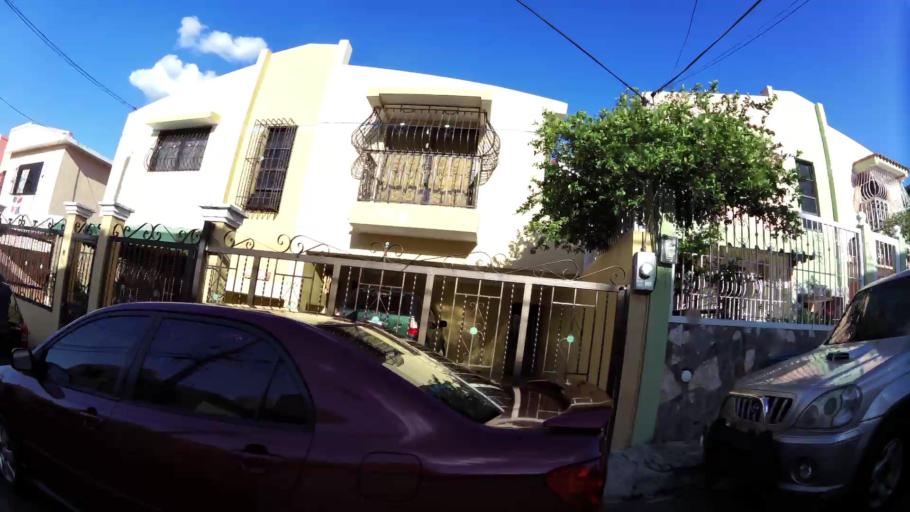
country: DO
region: Nacional
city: Santo Domingo
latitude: 18.4969
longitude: -69.9672
